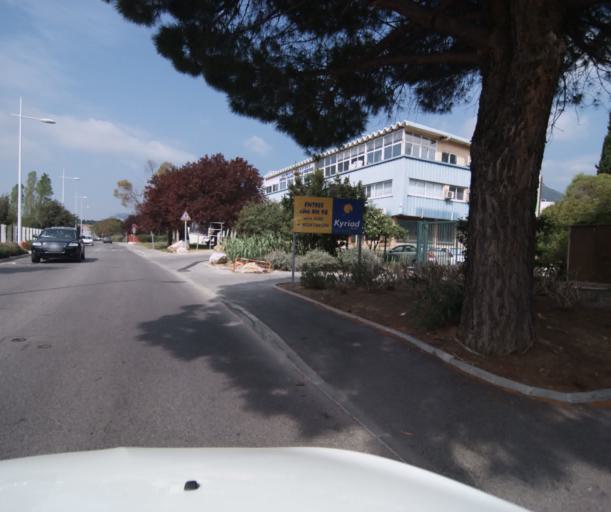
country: FR
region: Provence-Alpes-Cote d'Azur
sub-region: Departement du Var
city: La Garde
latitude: 43.1357
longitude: 6.0281
